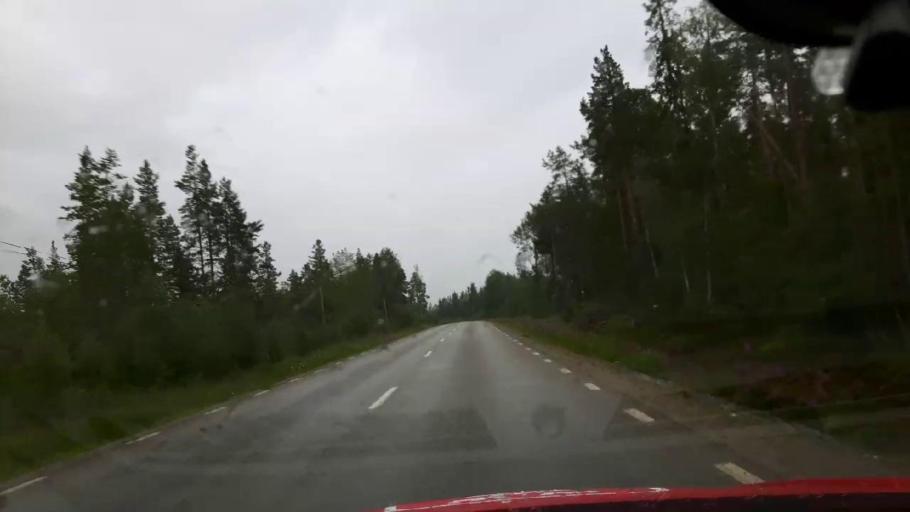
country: SE
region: Jaemtland
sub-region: OEstersunds Kommun
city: Brunflo
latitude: 62.7887
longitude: 15.0063
